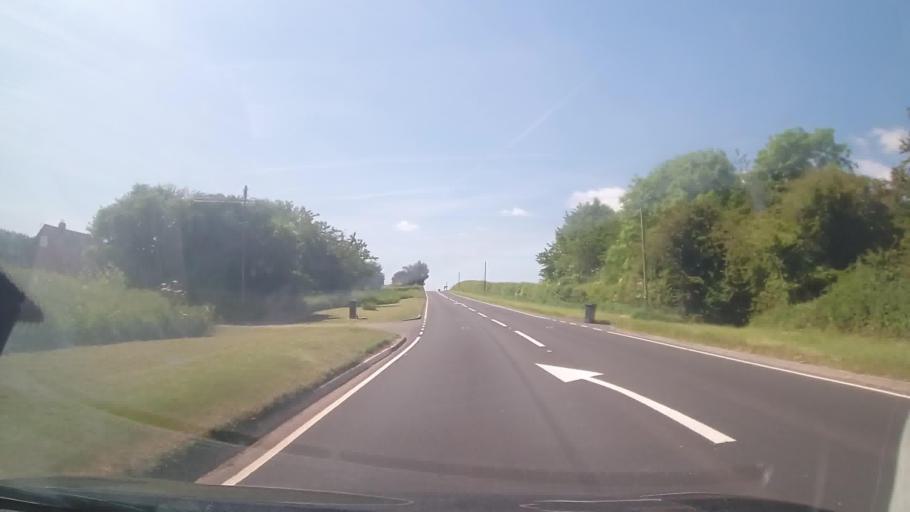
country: GB
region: England
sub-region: Herefordshire
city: Kimbolton
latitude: 52.2861
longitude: -2.7080
